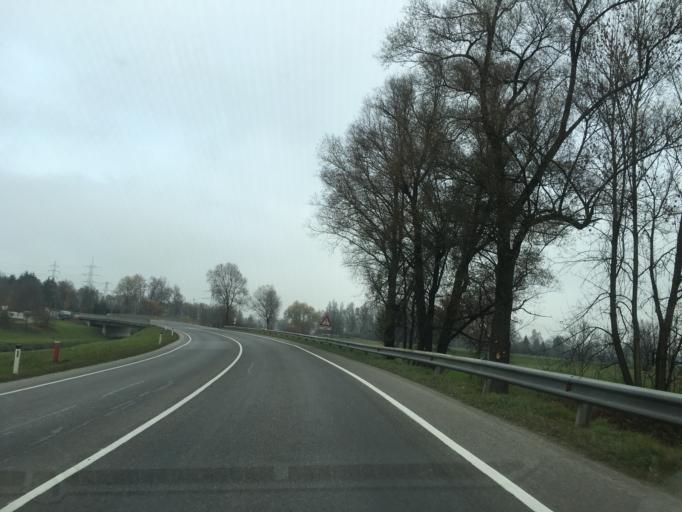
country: AT
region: Vorarlberg
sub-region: Politischer Bezirk Dornbirn
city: Hohenems
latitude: 47.3883
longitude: 9.6843
